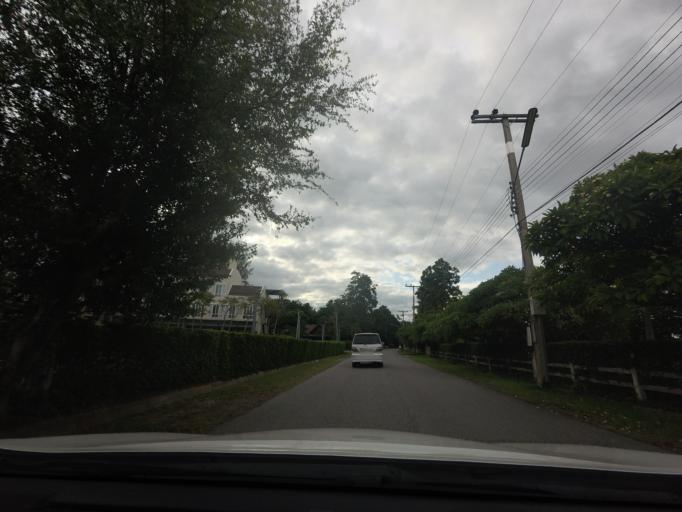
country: TH
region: Nakhon Ratchasima
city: Pak Chong
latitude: 14.5837
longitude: 101.4474
